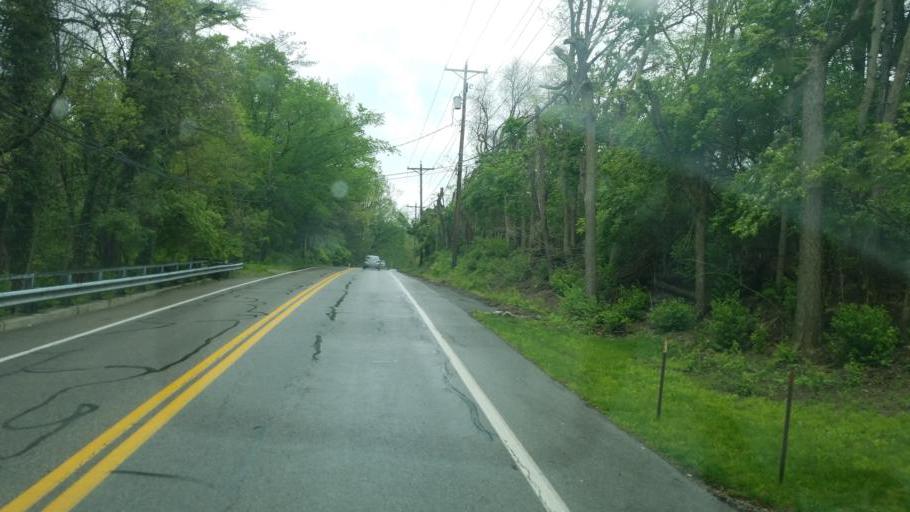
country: US
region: Ohio
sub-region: Franklin County
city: Worthington
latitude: 40.0935
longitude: -83.0496
